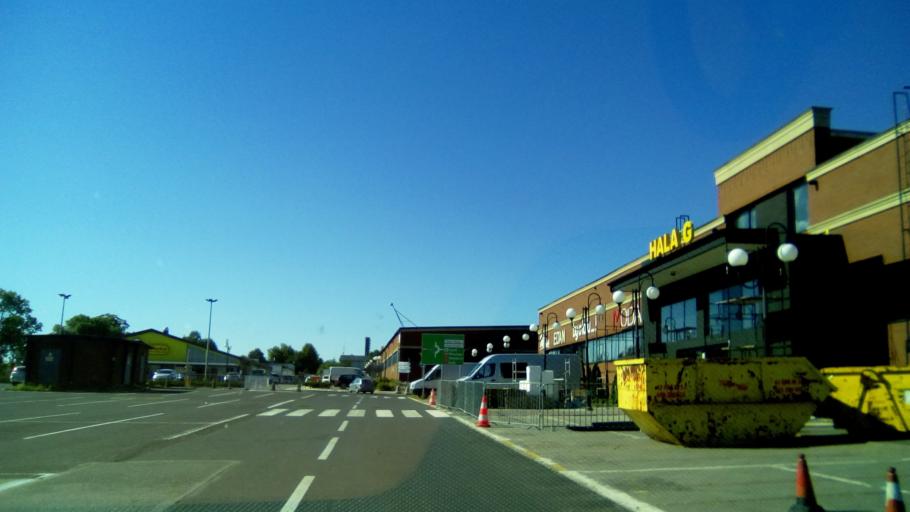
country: PL
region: Lodz Voivodeship
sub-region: Powiat lodzki wschodni
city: Rzgow
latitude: 51.6474
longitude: 19.4930
